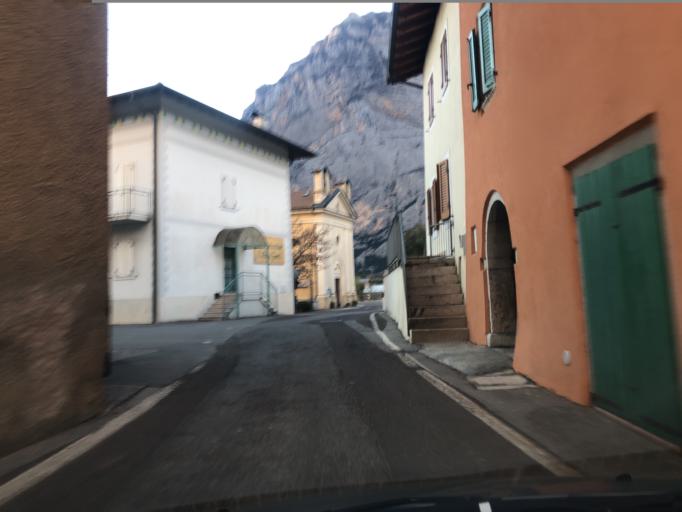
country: IT
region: Trentino-Alto Adige
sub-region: Provincia di Trento
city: Pietramurata
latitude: 46.0265
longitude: 10.9604
